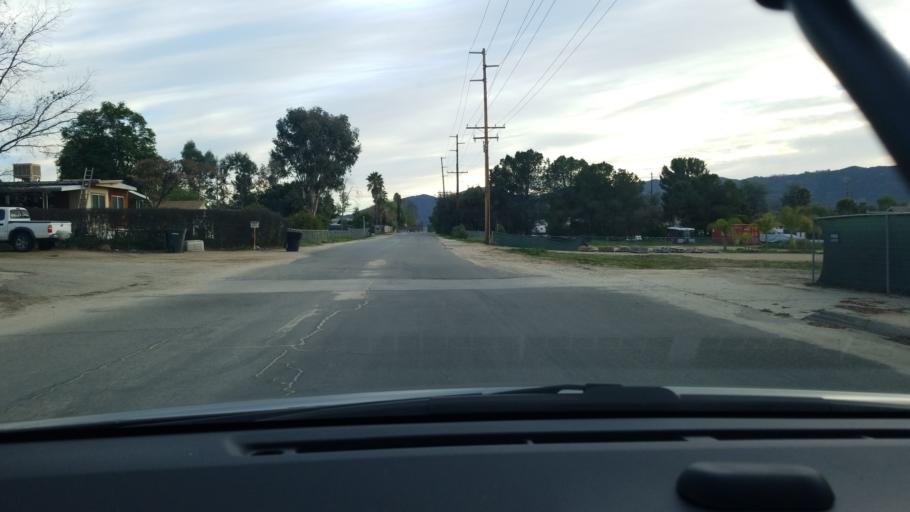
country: US
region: California
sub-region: Riverside County
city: Sedco Hills
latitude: 33.6326
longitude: -117.2796
